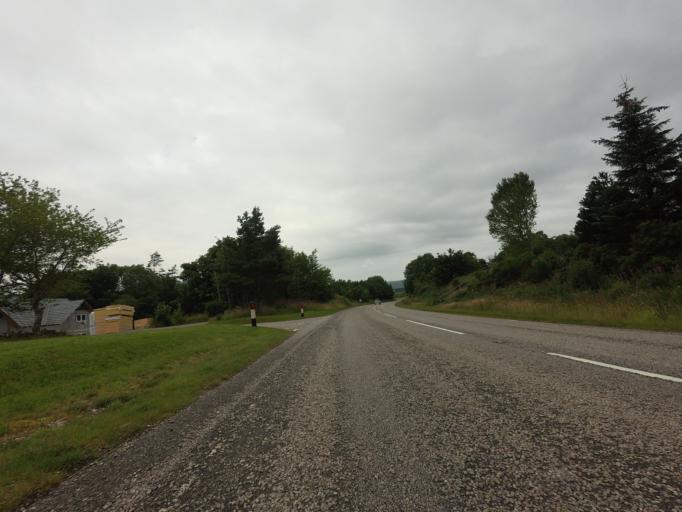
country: GB
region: Scotland
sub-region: Highland
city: Evanton
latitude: 57.9187
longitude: -4.3966
